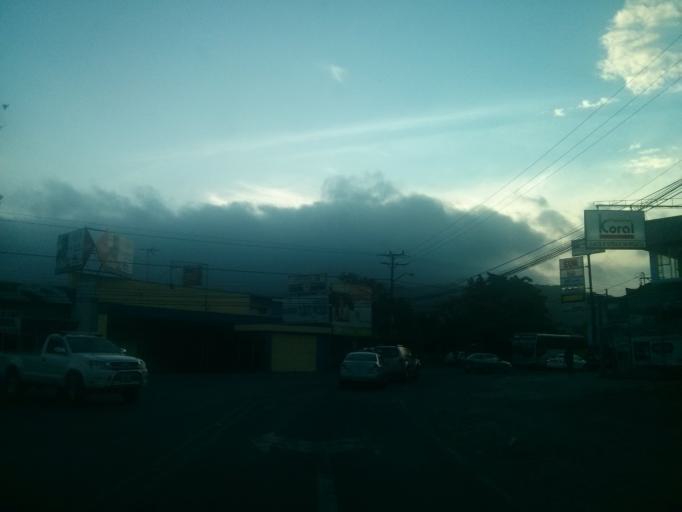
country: CR
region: Cartago
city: Cartago
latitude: 9.8810
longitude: -83.9352
